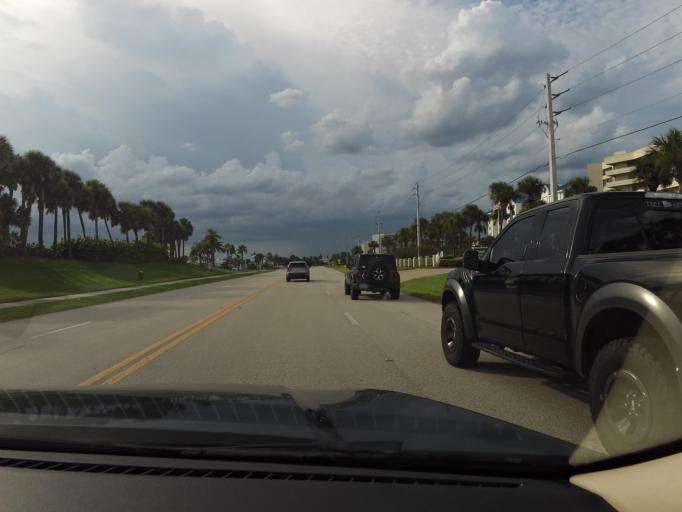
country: US
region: Florida
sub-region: Volusia County
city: Ponce Inlet
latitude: 29.1018
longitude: -80.9400
